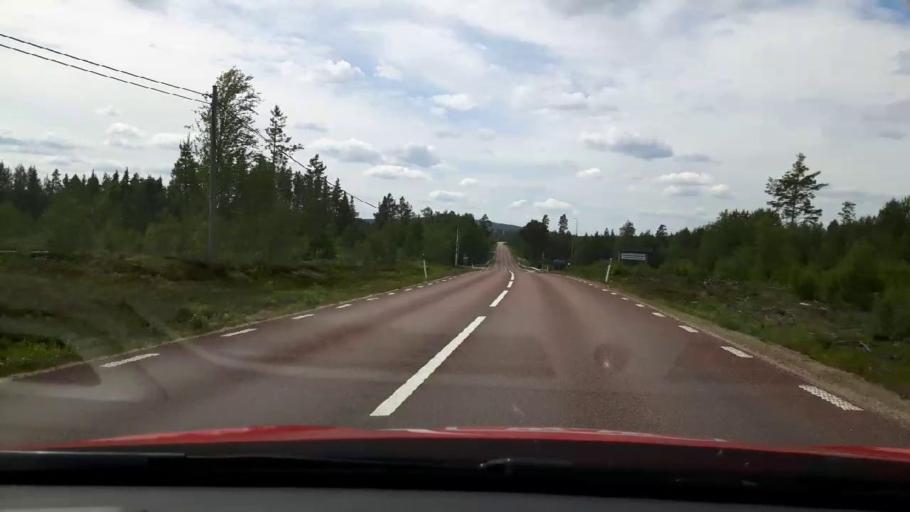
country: SE
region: Jaemtland
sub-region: Harjedalens Kommun
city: Sveg
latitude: 62.0460
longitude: 14.4770
